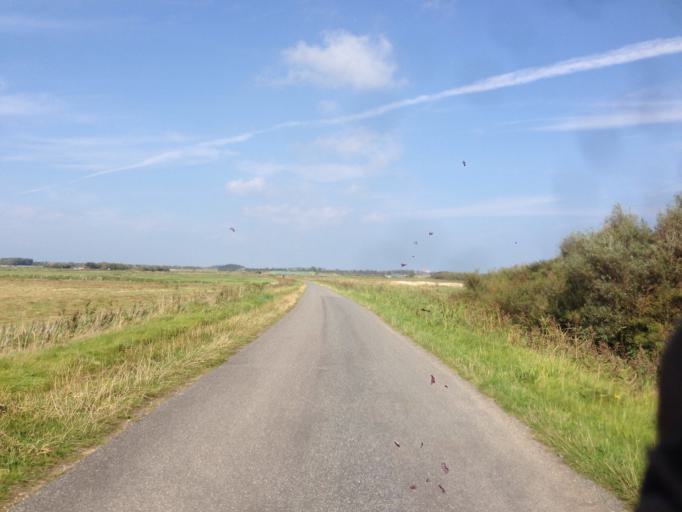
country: DE
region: Schleswig-Holstein
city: Tinnum
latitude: 54.8825
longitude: 8.3416
